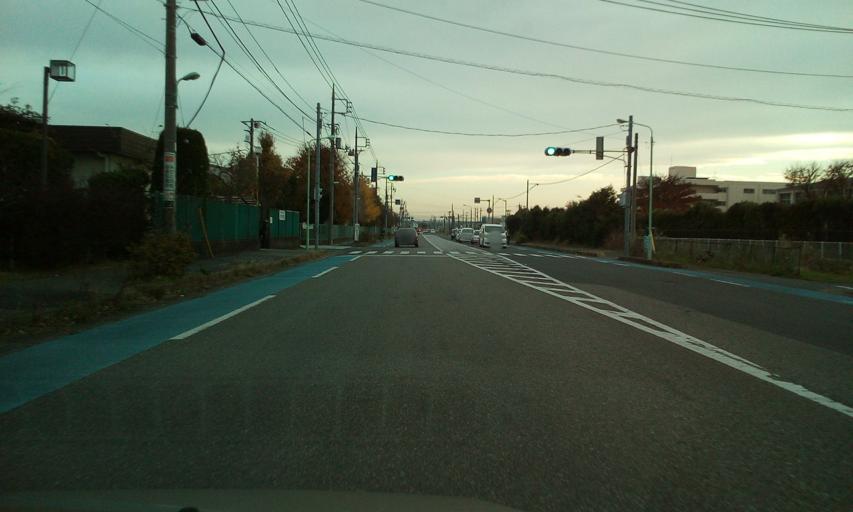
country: JP
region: Saitama
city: Yoshikawa
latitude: 35.8541
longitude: 139.8601
